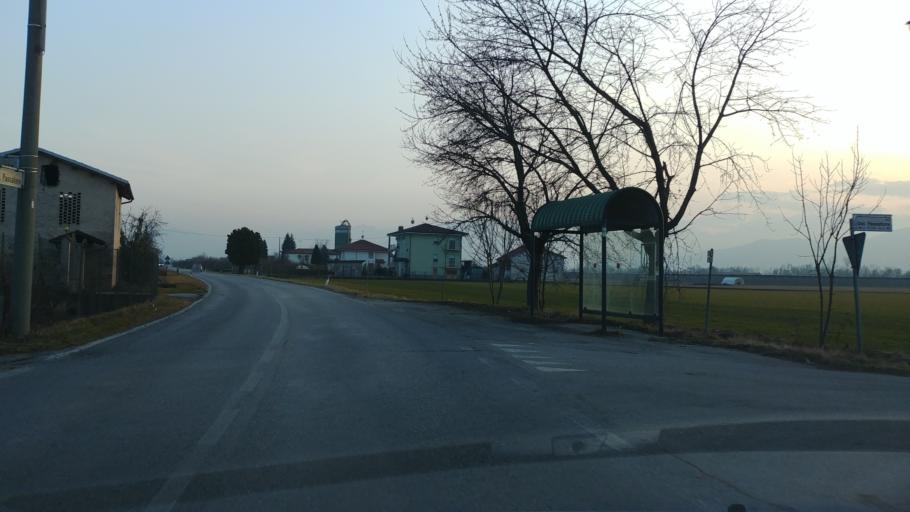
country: IT
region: Piedmont
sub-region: Provincia di Cuneo
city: Roata Rossi
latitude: 44.4245
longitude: 7.5066
